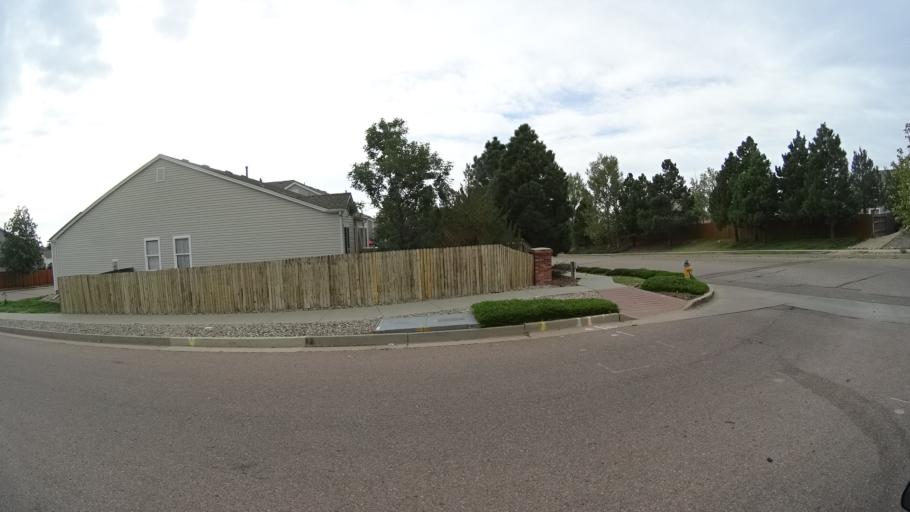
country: US
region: Colorado
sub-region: El Paso County
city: Cimarron Hills
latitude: 38.9131
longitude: -104.7058
